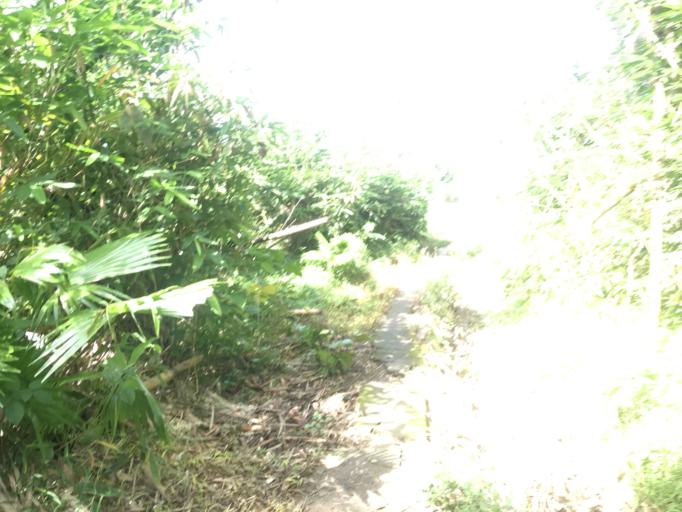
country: PH
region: Calabarzon
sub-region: Province of Quezon
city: Macalelon
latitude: 13.7810
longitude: 122.1431
